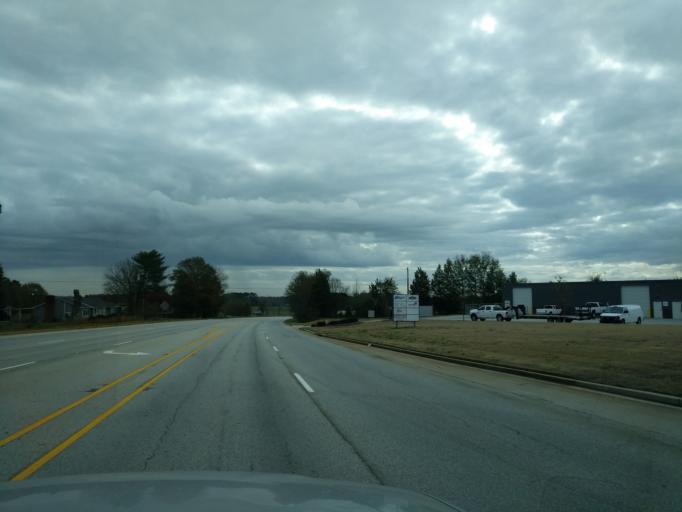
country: US
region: South Carolina
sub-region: Spartanburg County
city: Roebuck
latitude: 34.8742
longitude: -82.0383
